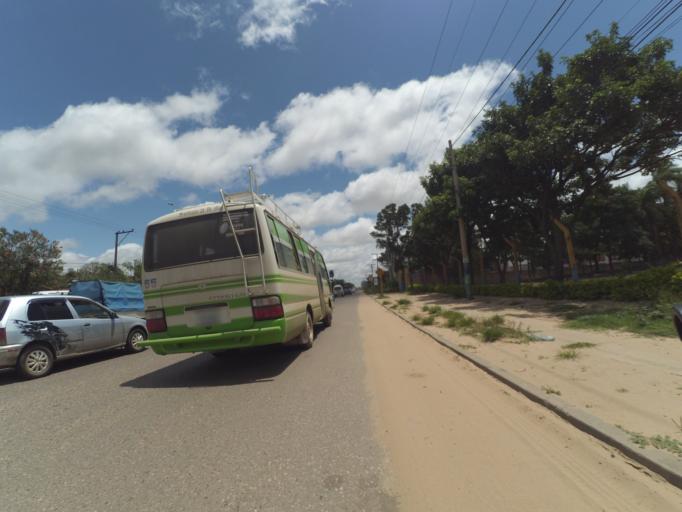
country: BO
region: Santa Cruz
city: Santa Cruz de la Sierra
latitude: -17.8371
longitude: -63.2367
